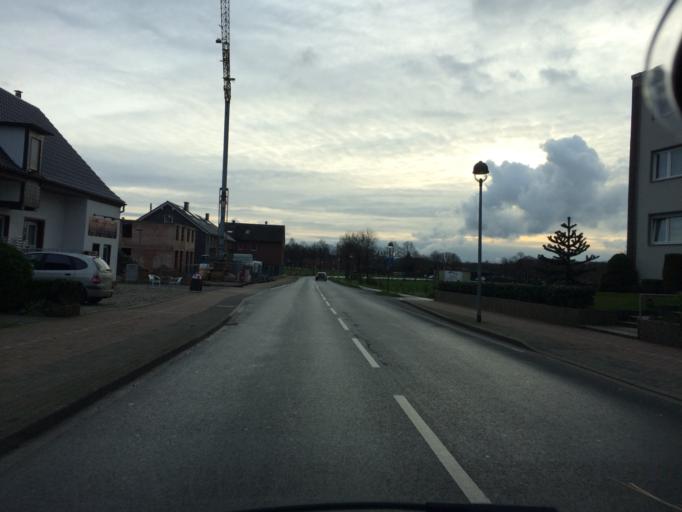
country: DE
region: North Rhine-Westphalia
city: Marl
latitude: 51.7134
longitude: 7.0944
